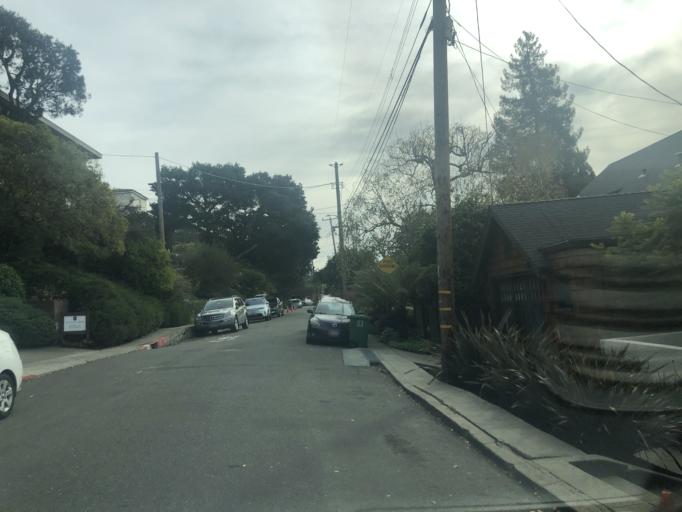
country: US
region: California
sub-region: Alameda County
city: Piedmont
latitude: 37.8558
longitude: -122.2421
